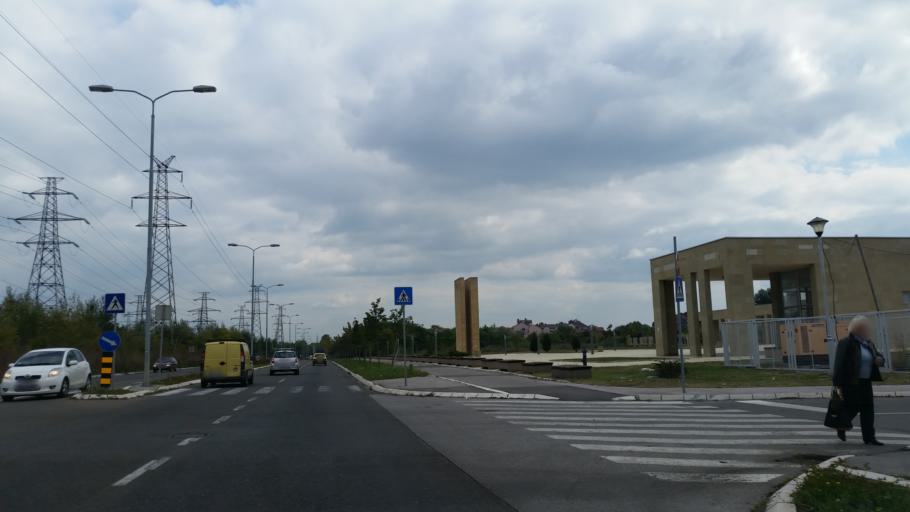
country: RS
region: Central Serbia
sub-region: Belgrade
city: Zemun
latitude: 44.8221
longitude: 20.3669
